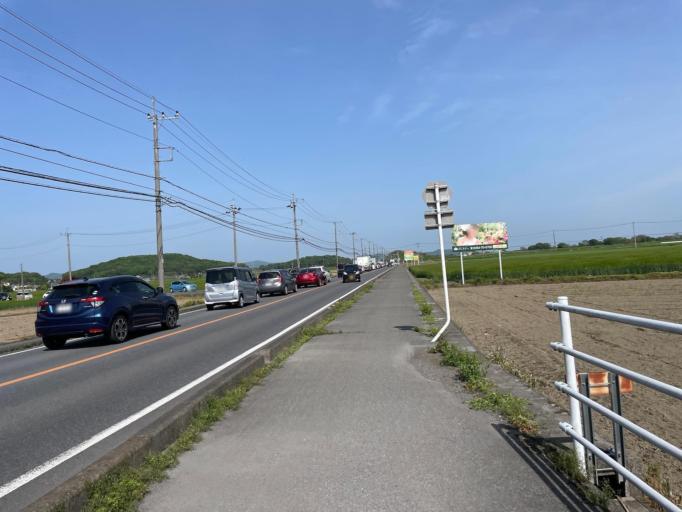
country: JP
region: Gunma
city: Tatebayashi
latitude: 36.3051
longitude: 139.5156
